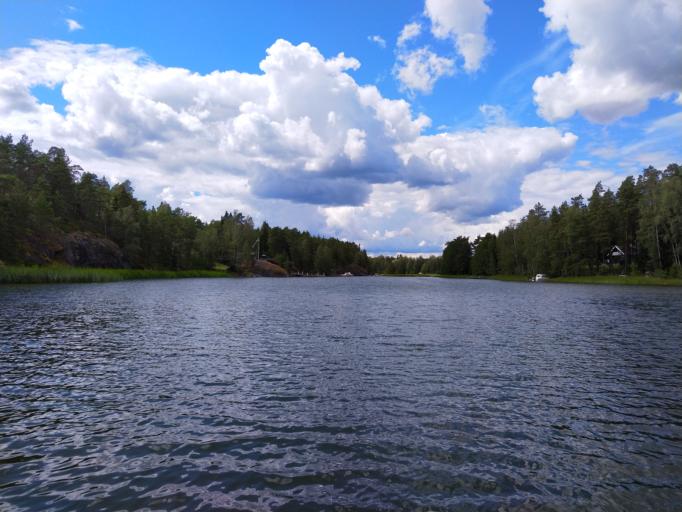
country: FI
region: Uusimaa
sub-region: Raaseporin
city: Karis
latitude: 59.9705
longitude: 23.7132
